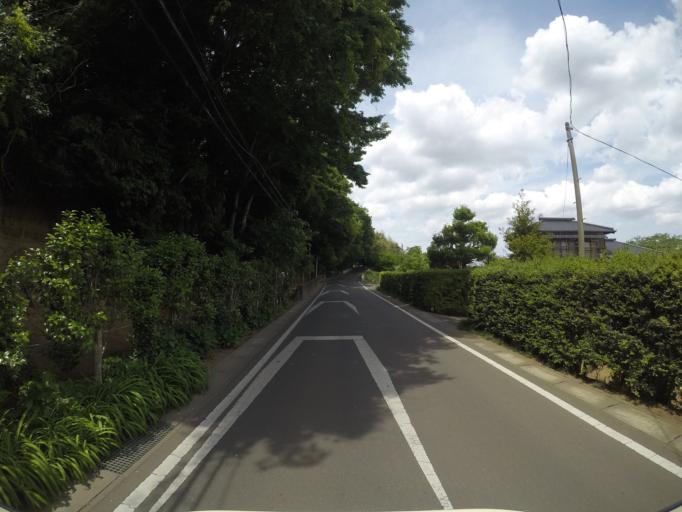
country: JP
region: Ibaraki
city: Ushiku
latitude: 35.9660
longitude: 140.1199
